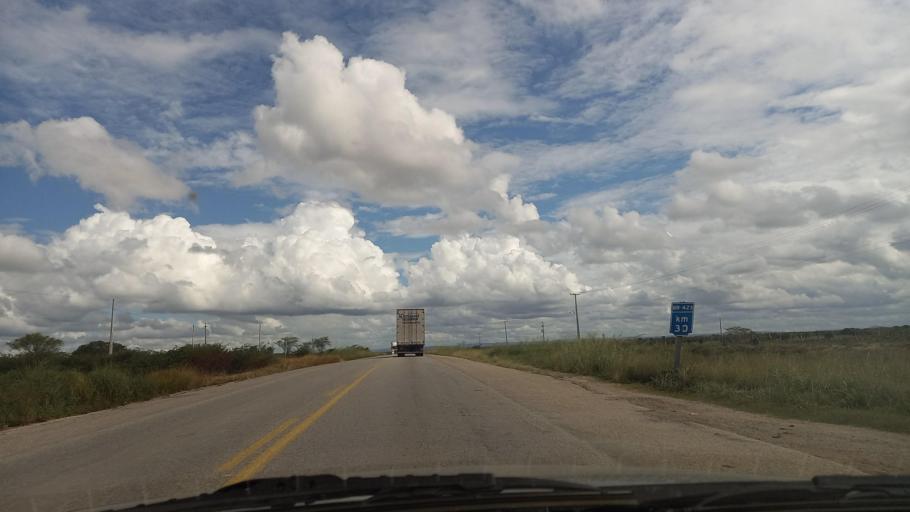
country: BR
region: Pernambuco
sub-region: Cachoeirinha
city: Cachoeirinha
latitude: -8.4180
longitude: -36.1931
